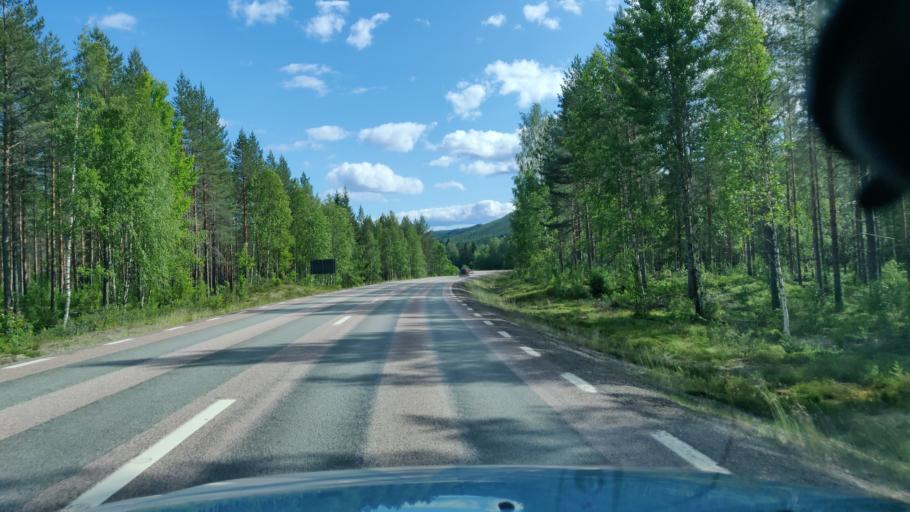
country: SE
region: Vaermland
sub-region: Torsby Kommun
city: Torsby
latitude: 60.5276
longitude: 13.1305
